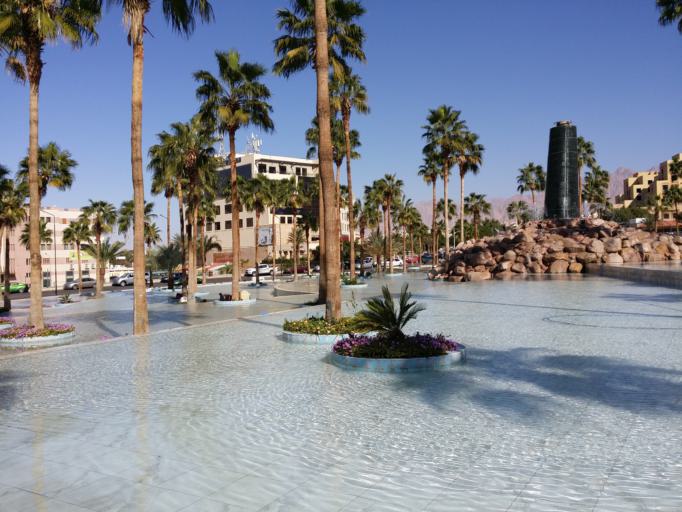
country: JO
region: Aqaba
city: Aqaba
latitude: 29.5318
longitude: 35.0059
